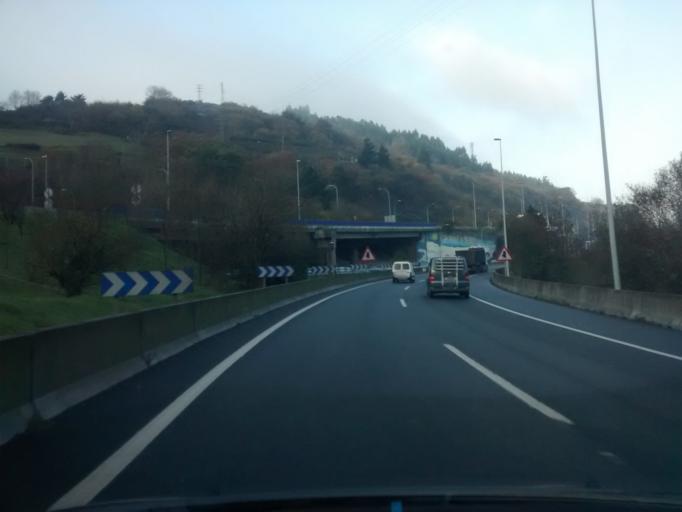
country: ES
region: Basque Country
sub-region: Bizkaia
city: Santutxu
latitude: 43.2333
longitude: -2.9142
